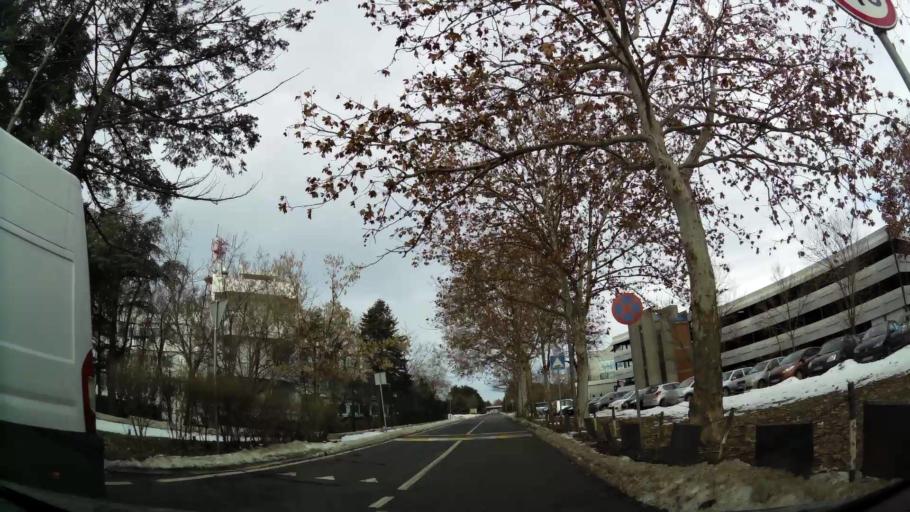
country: RS
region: Central Serbia
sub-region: Belgrade
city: Surcin
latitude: 44.8178
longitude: 20.2887
